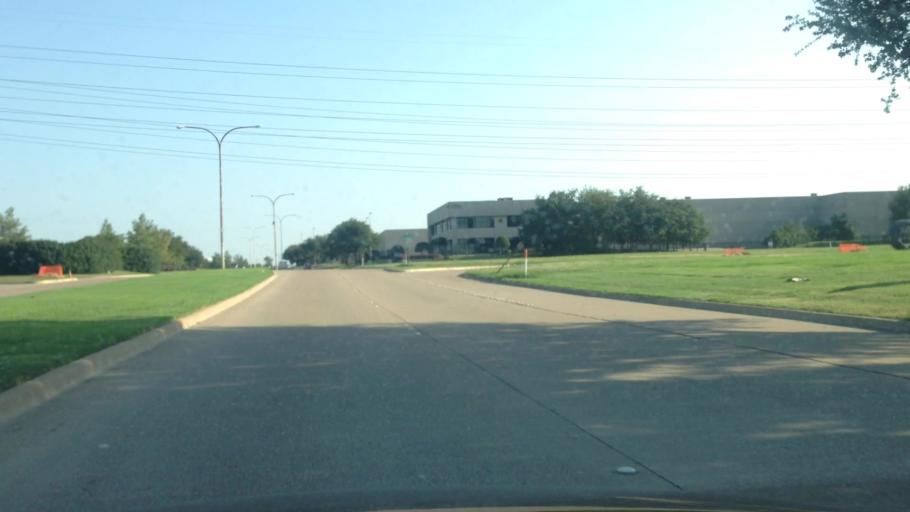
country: US
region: Texas
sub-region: Tarrant County
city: Haltom City
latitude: 32.8217
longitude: -97.3085
